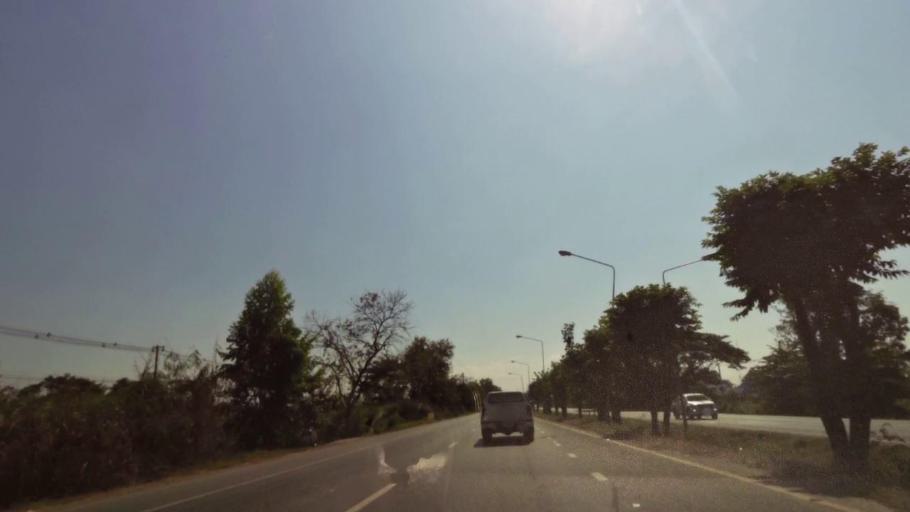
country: TH
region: Nakhon Sawan
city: Kao Liao
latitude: 15.7969
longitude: 100.1206
